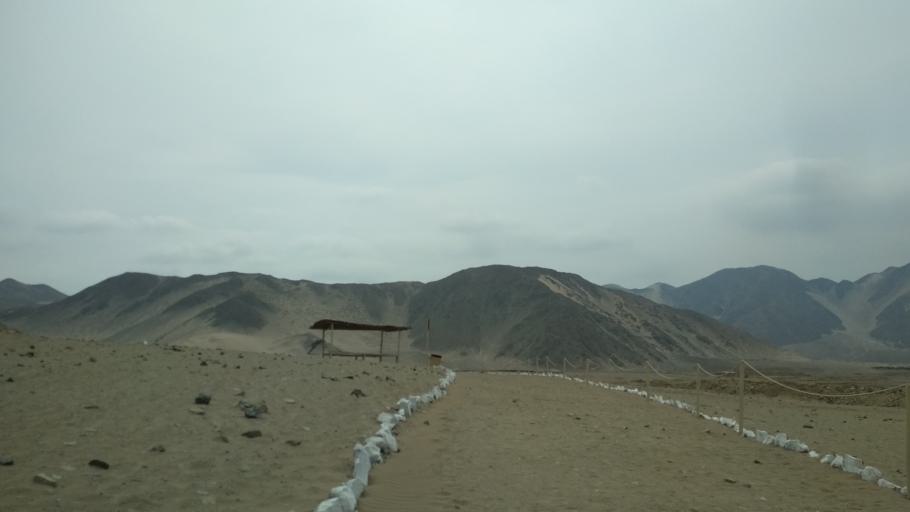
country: PE
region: Lima
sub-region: Huaura
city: Vegueta
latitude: -10.8936
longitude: -77.5181
